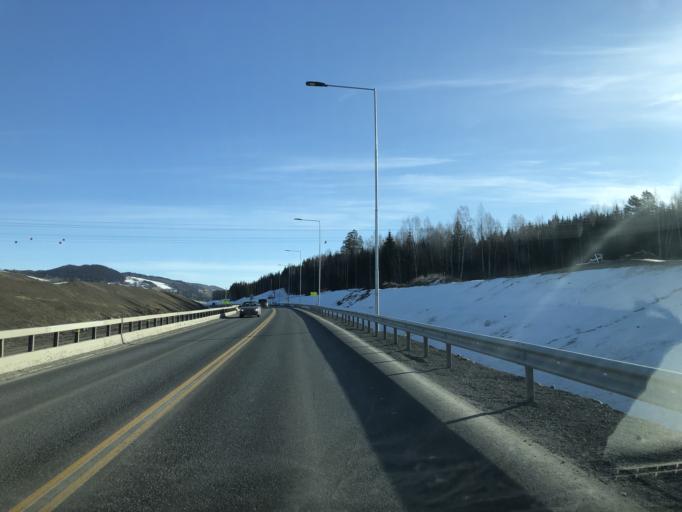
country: NO
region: Hedmark
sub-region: Ringsaker
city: Moelv
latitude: 60.9092
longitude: 10.7426
